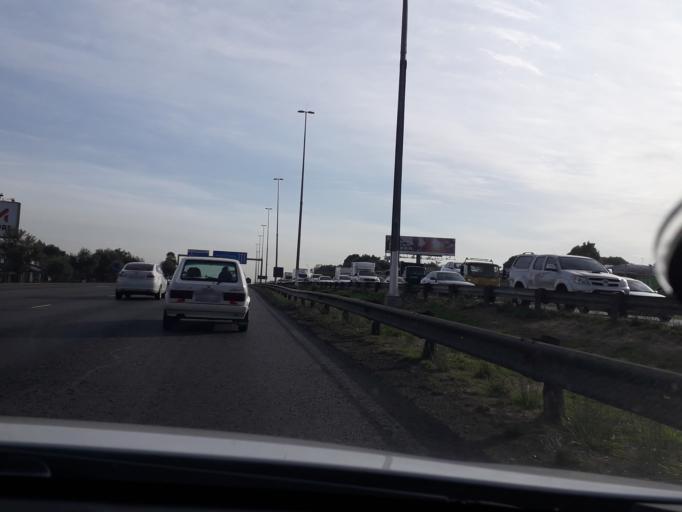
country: ZA
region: Gauteng
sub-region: City of Johannesburg Metropolitan Municipality
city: Modderfontein
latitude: -26.1604
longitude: 28.1588
